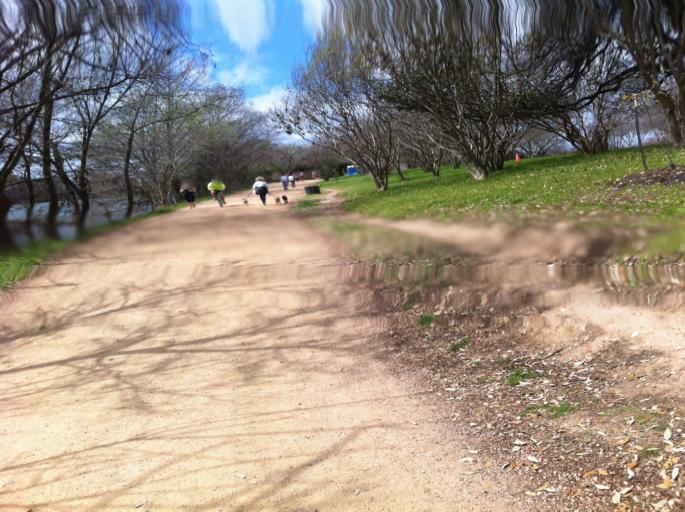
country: US
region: Texas
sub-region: Travis County
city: Austin
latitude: 30.2670
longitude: -97.7576
